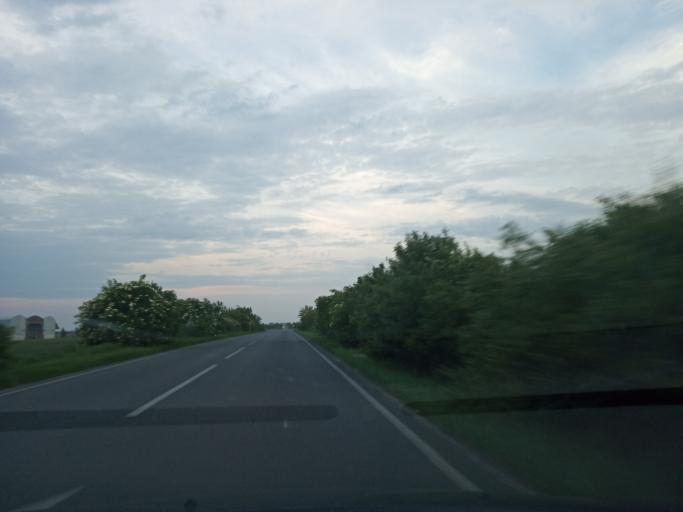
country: RO
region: Timis
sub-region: Comuna Voiteg
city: Voiteg
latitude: 45.4522
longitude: 21.2339
